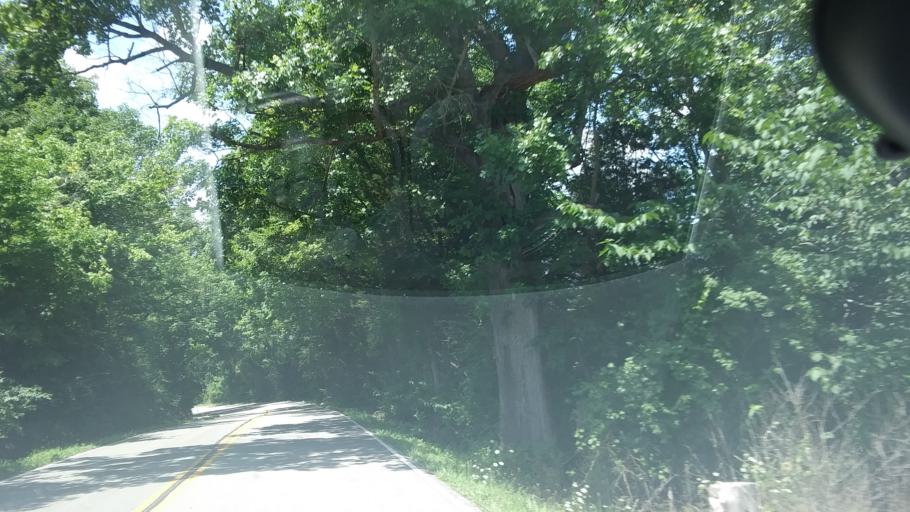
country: US
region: Tennessee
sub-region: Davidson County
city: Belle Meade
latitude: 36.1210
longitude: -86.9200
